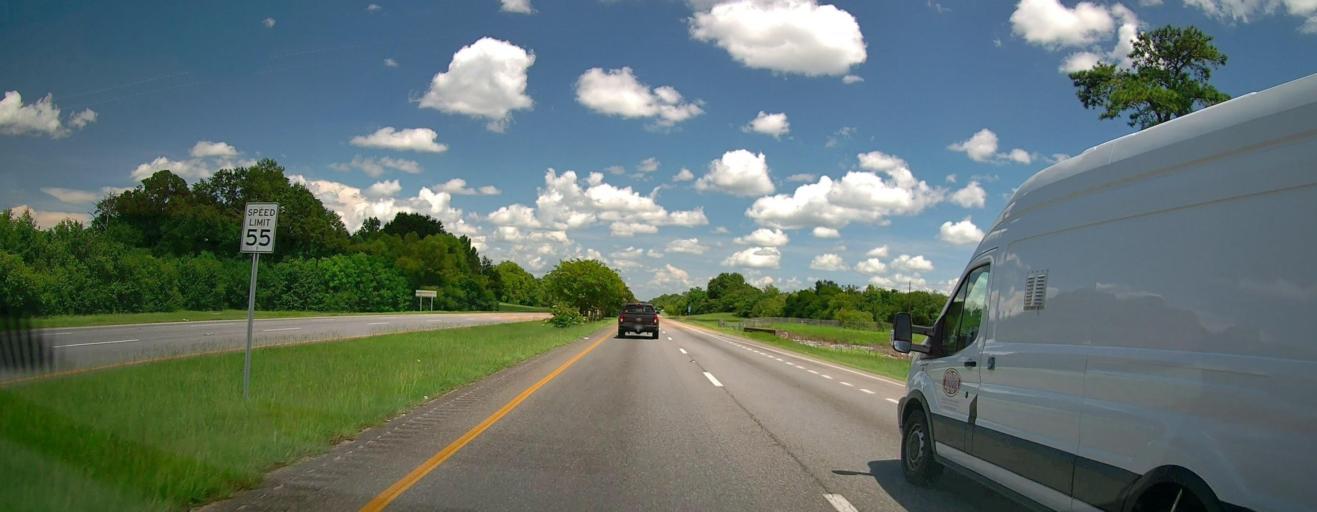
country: US
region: Alabama
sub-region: Montgomery County
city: Montgomery
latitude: 32.4226
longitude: -86.2657
